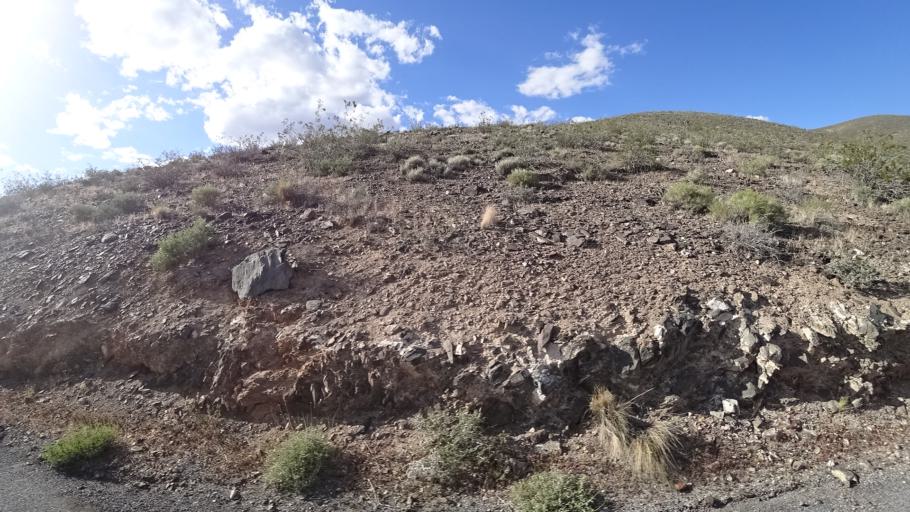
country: US
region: California
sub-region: San Bernardino County
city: Searles Valley
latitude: 36.3082
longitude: -117.1490
